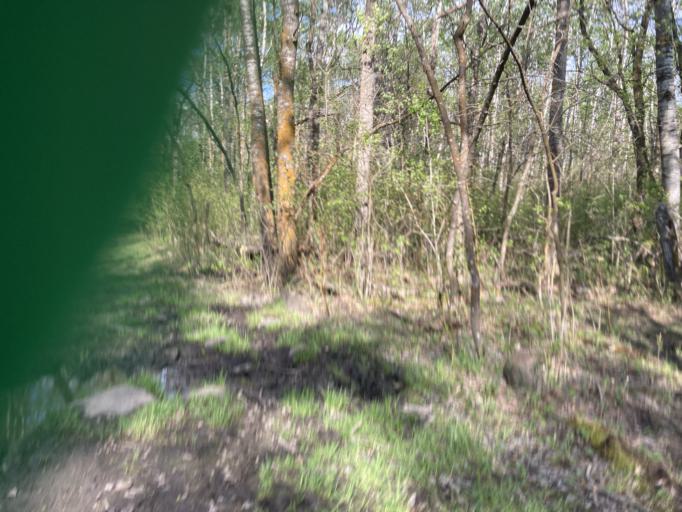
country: CA
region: Manitoba
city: Brandon
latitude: 49.7193
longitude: -99.8987
